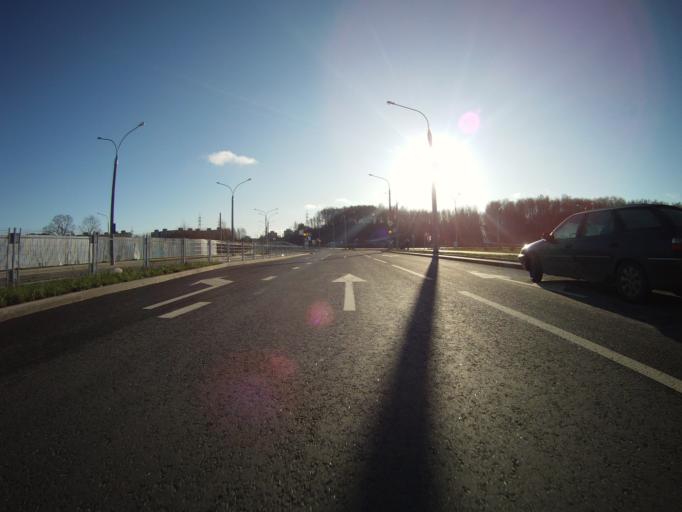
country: BY
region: Minsk
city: Novoye Medvezhino
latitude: 53.8739
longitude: 27.4558
